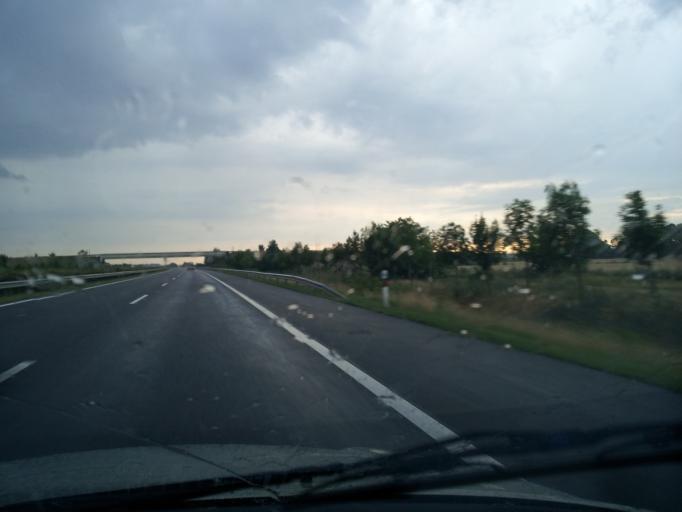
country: HU
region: Heves
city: Szihalom
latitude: 47.7691
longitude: 20.5258
